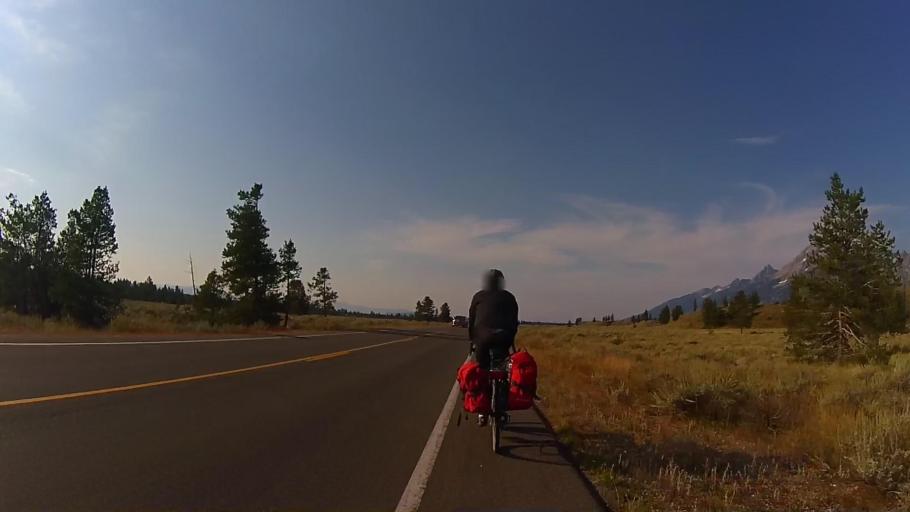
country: US
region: Wyoming
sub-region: Teton County
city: Moose Wilson Road
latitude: 43.7989
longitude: -110.6864
